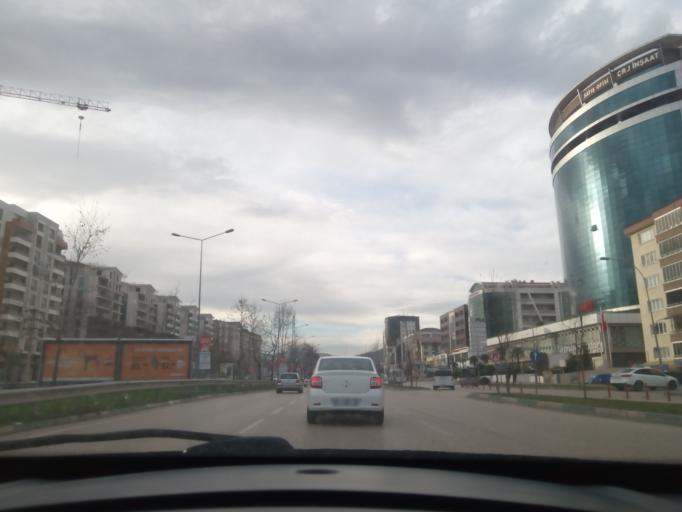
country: TR
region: Bursa
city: Cali
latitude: 40.2202
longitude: 28.9523
